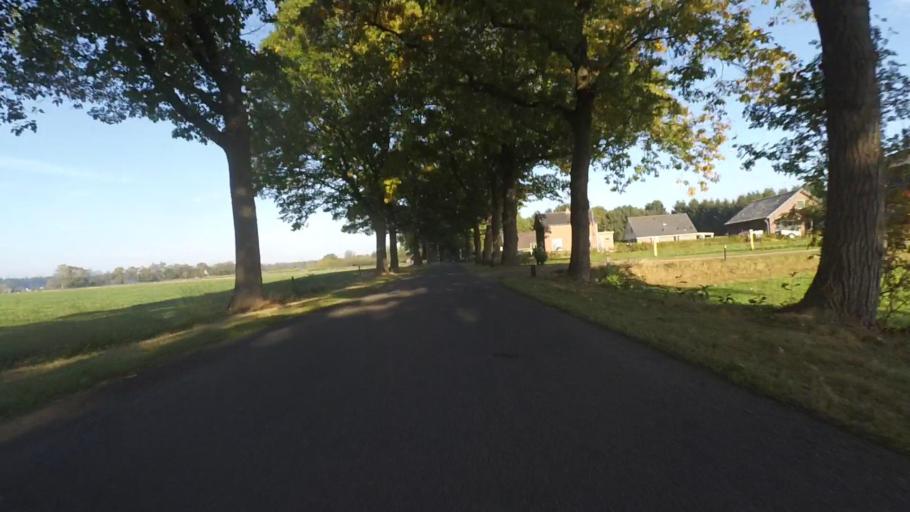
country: NL
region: Gelderland
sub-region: Gemeente Epe
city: Vaassen
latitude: 52.2987
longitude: 5.9484
